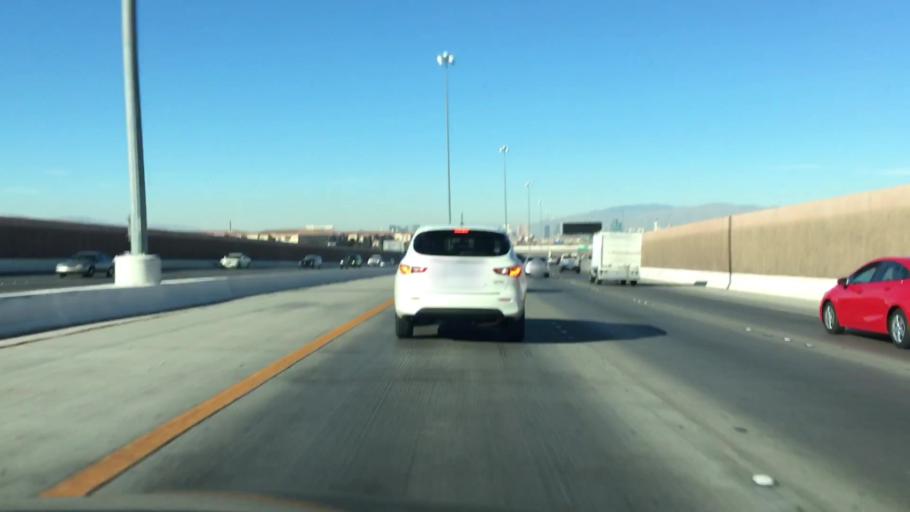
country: US
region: Nevada
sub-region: Clark County
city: Whitney
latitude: 36.0297
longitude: -115.1311
